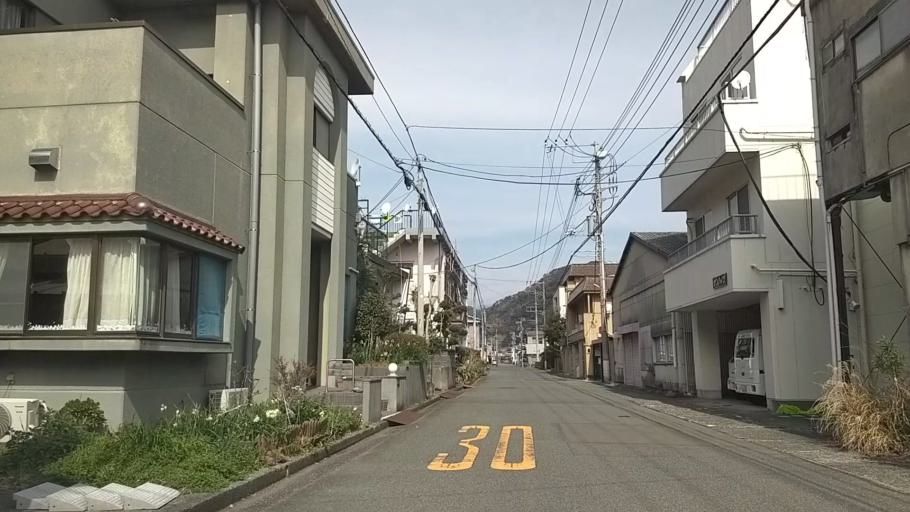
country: JP
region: Shizuoka
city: Shimoda
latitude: 34.6823
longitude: 138.9433
